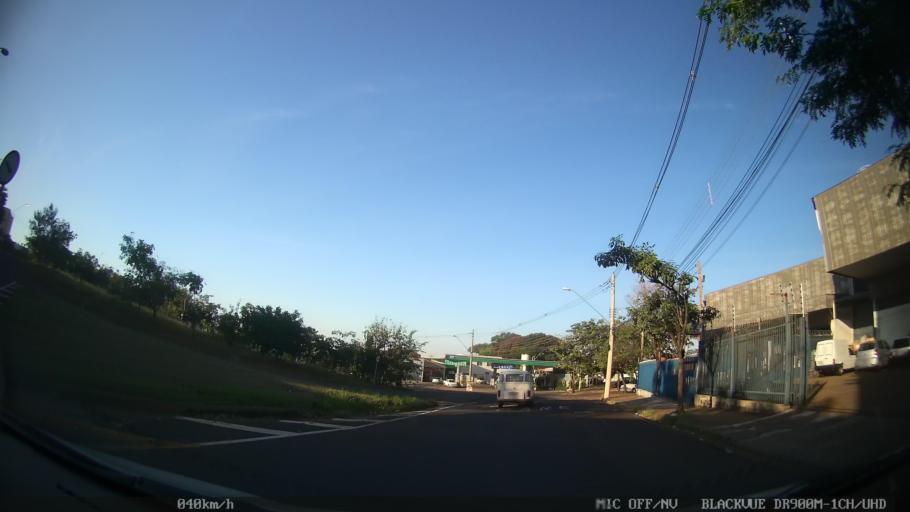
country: BR
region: Sao Paulo
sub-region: Sao Jose Do Rio Preto
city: Sao Jose do Rio Preto
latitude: -20.7938
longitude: -49.3536
